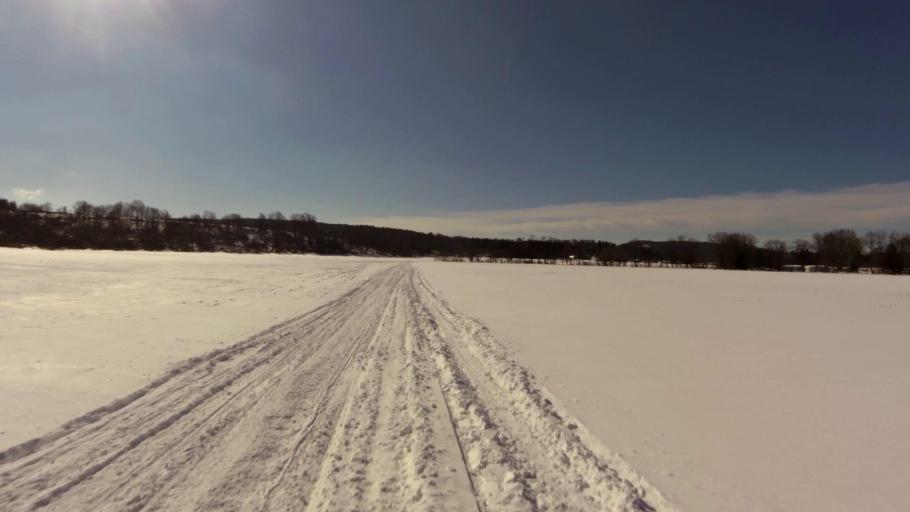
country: US
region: New York
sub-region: Cattaraugus County
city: Franklinville
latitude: 42.3514
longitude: -78.4498
